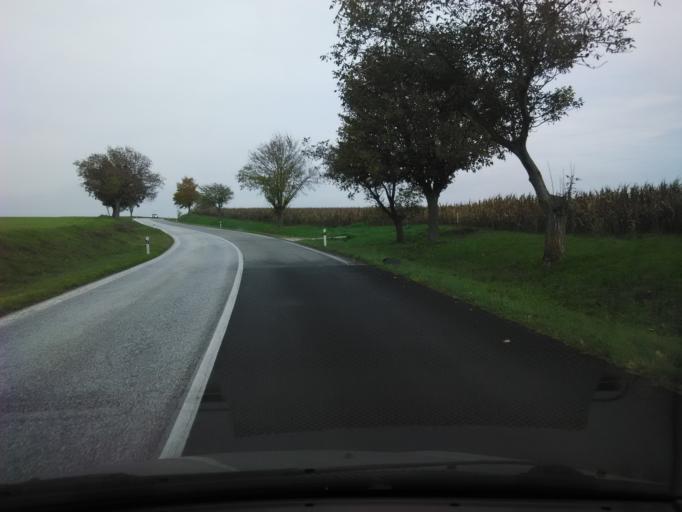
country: SK
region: Nitriansky
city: Svodin
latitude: 48.0047
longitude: 18.3724
